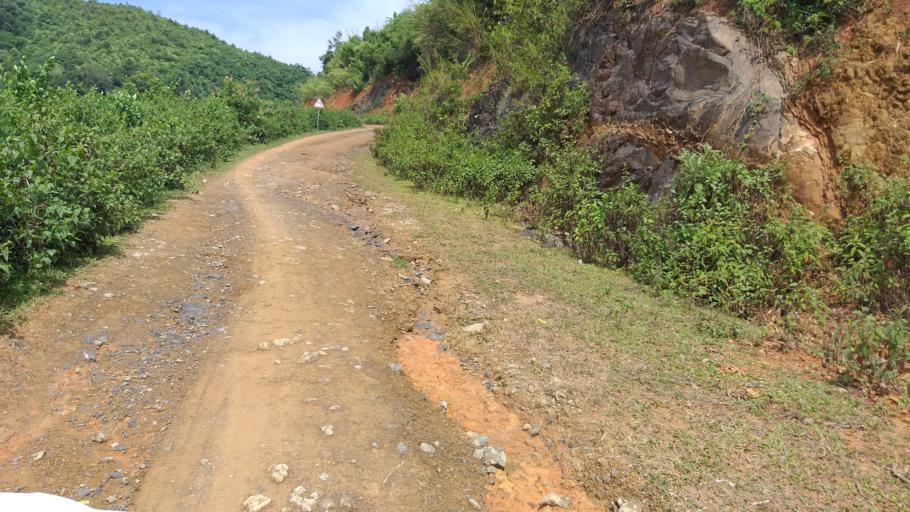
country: VN
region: Huyen Dien Bien
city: Dien Bien Phu
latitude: 21.4176
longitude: 102.6834
